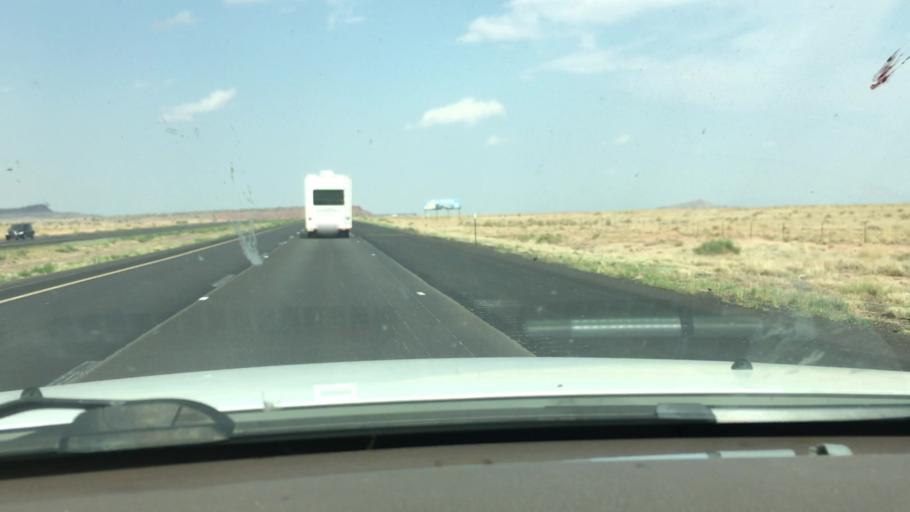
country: US
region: New Mexico
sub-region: Cibola County
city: Laguna
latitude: 34.9929
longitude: -107.2409
